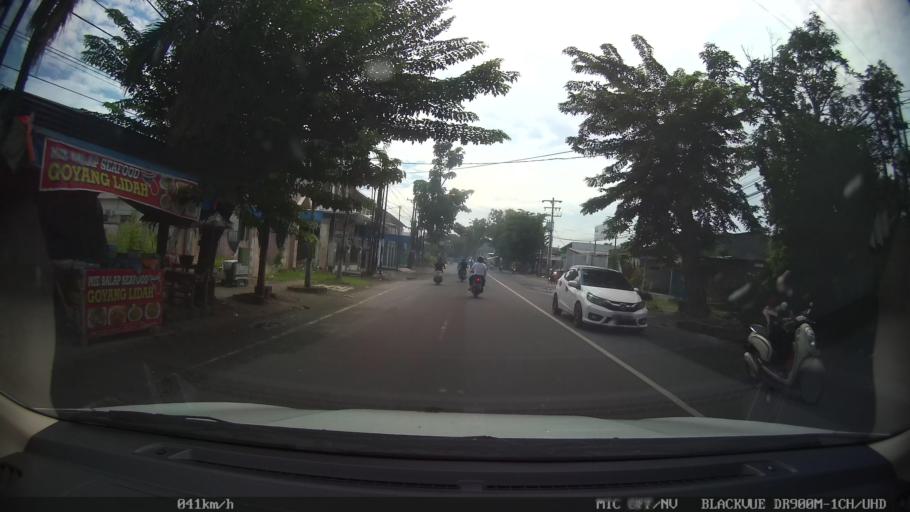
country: ID
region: North Sumatra
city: Medan
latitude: 3.6225
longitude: 98.6900
